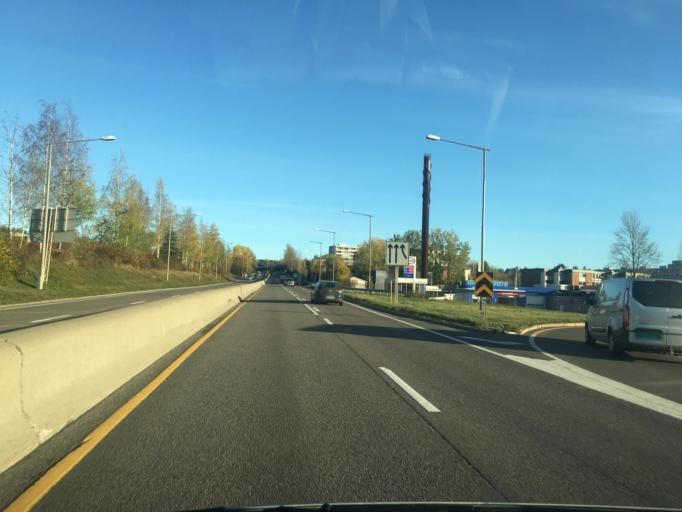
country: NO
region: Akershus
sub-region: Lorenskog
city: Kjenn
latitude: 59.9535
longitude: 10.9093
